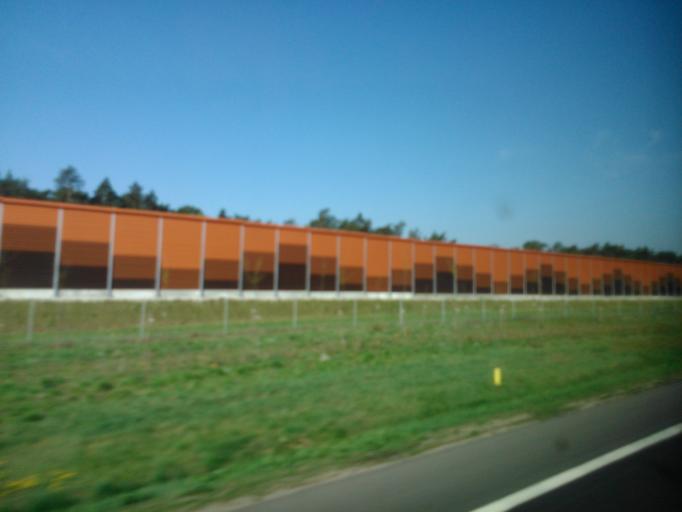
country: PL
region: Kujawsko-Pomorskie
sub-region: Powiat aleksandrowski
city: Ciechocinek
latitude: 52.8766
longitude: 18.7485
